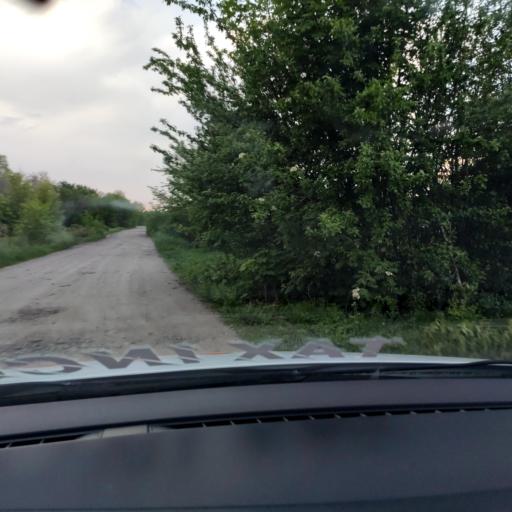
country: RU
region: Voronezj
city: Kolodeznyy
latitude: 51.4355
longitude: 39.2321
